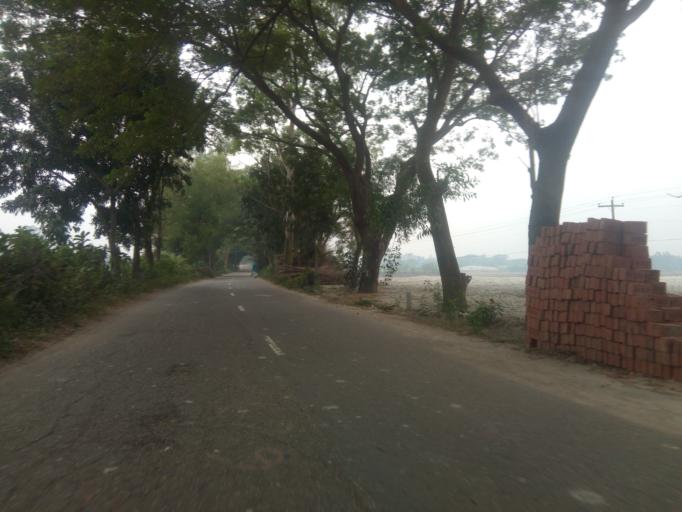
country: BD
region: Dhaka
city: Narayanganj
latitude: 23.5207
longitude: 90.4712
